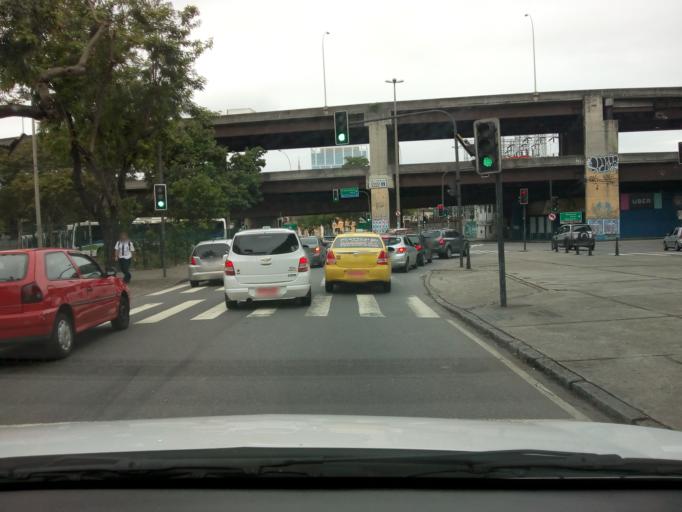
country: BR
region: Rio de Janeiro
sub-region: Rio De Janeiro
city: Rio de Janeiro
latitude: -22.8984
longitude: -43.2196
